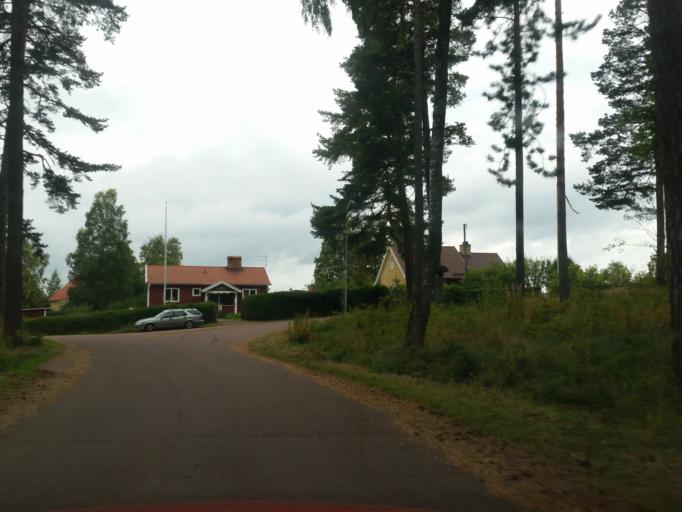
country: SE
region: Dalarna
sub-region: Leksand Municipality
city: Smedby
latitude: 60.6753
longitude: 15.1036
